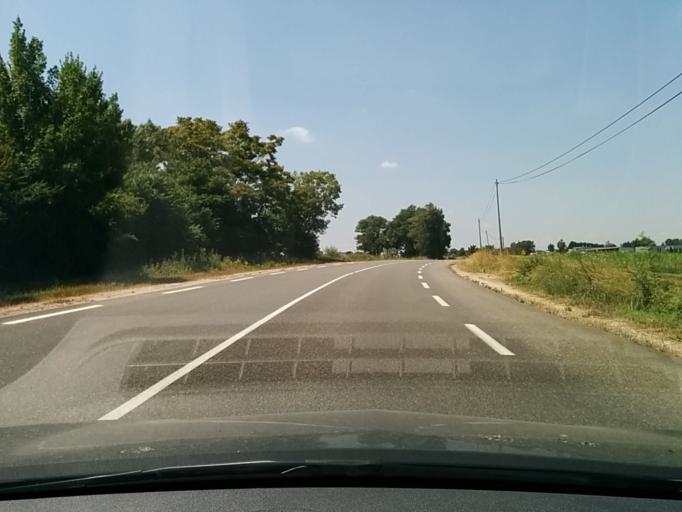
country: FR
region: Midi-Pyrenees
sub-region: Departement du Gers
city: Pujaudran
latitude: 43.6016
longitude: 1.0289
